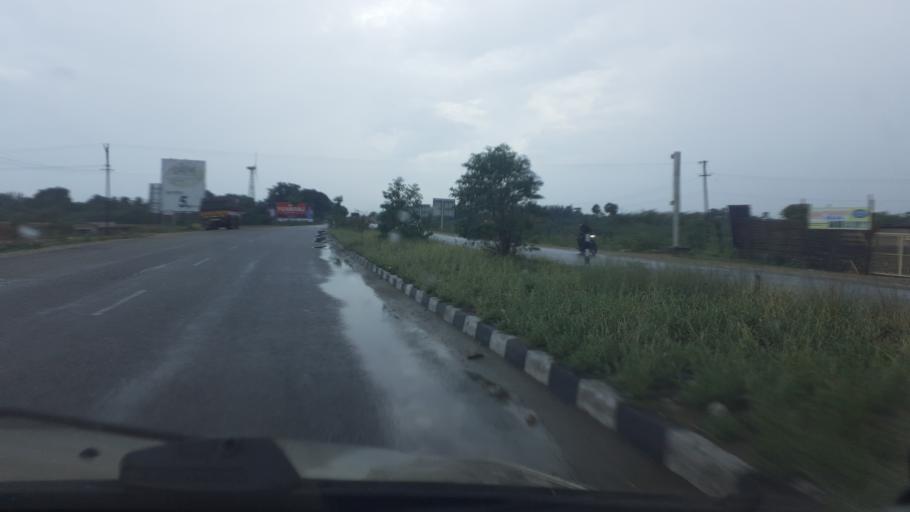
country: IN
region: Tamil Nadu
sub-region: Thoothukkudi
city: Kayattar
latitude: 8.9738
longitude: 77.7745
